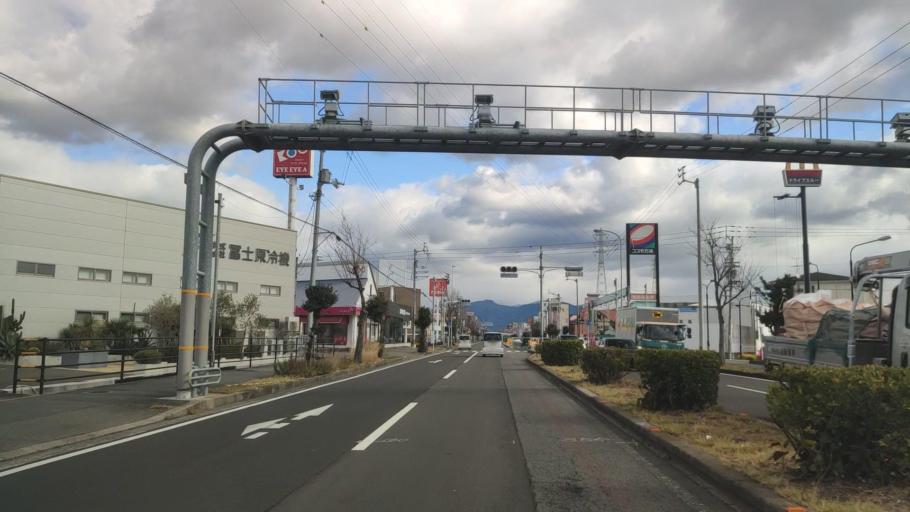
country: JP
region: Ehime
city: Masaki-cho
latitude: 33.8130
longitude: 132.7376
